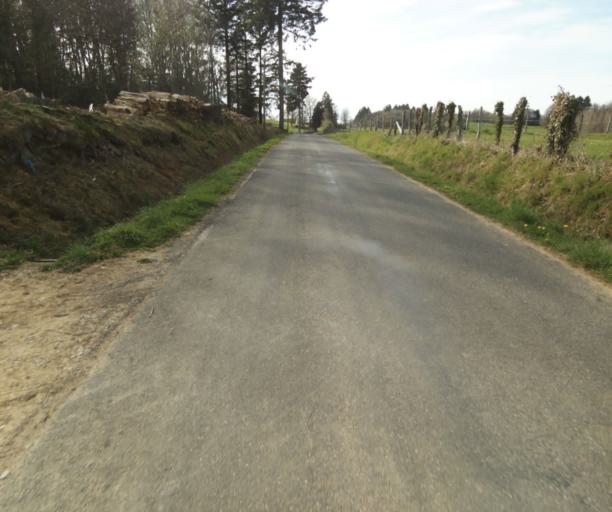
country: FR
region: Limousin
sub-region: Departement de la Correze
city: Seilhac
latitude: 45.3309
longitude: 1.7291
